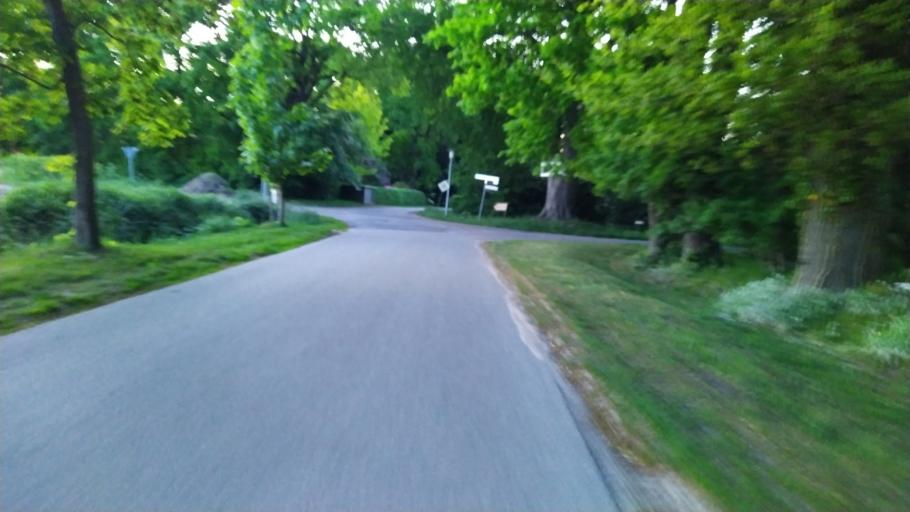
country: DE
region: Lower Saxony
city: Bargstedt
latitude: 53.4819
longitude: 9.4657
